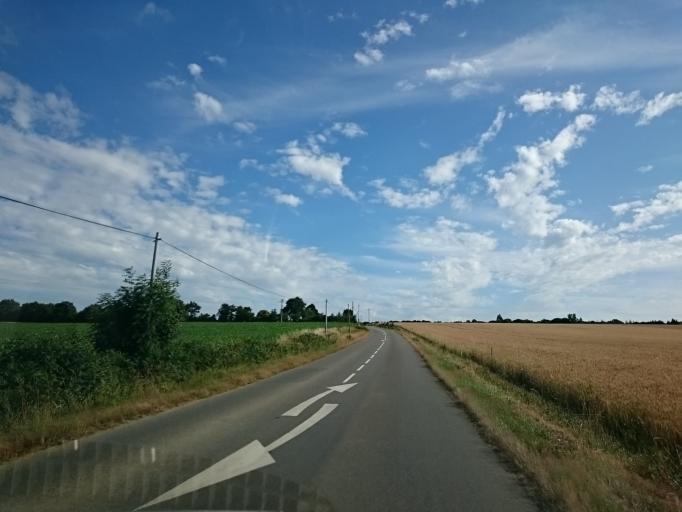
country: FR
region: Brittany
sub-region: Departement d'Ille-et-Vilaine
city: Chanteloup
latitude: 47.9217
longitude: -1.6180
